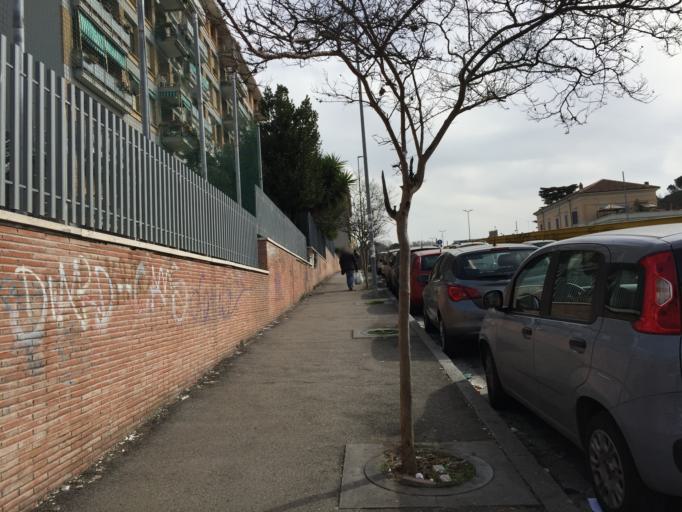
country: VA
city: Vatican City
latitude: 41.8973
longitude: 12.4542
